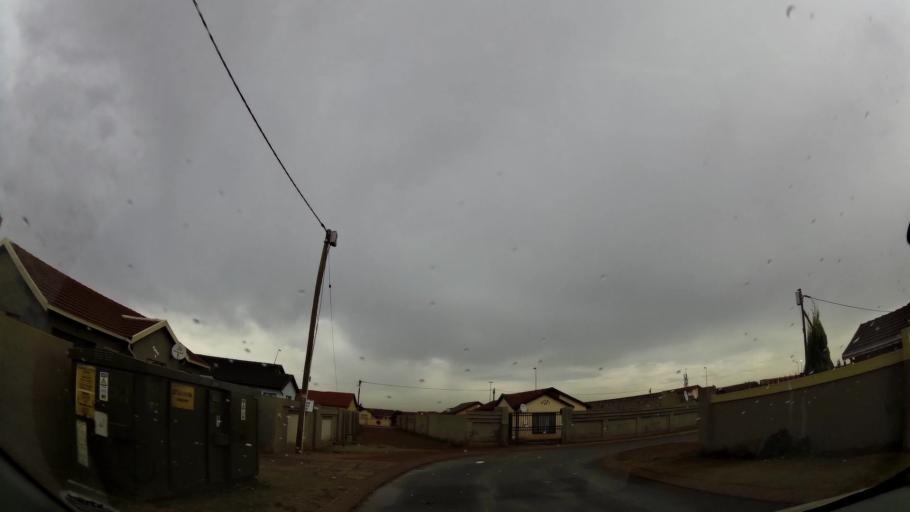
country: ZA
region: Gauteng
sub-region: Ekurhuleni Metropolitan Municipality
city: Germiston
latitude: -26.3338
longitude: 28.1989
